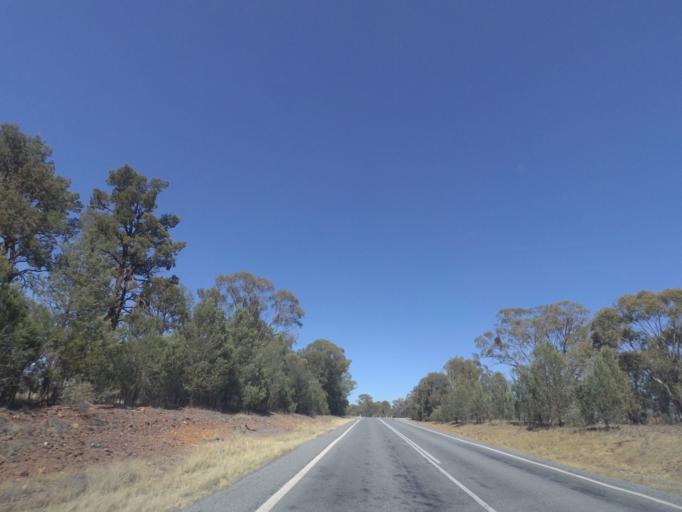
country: AU
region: New South Wales
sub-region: Narrandera
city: Narrandera
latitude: -34.4183
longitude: 146.8506
